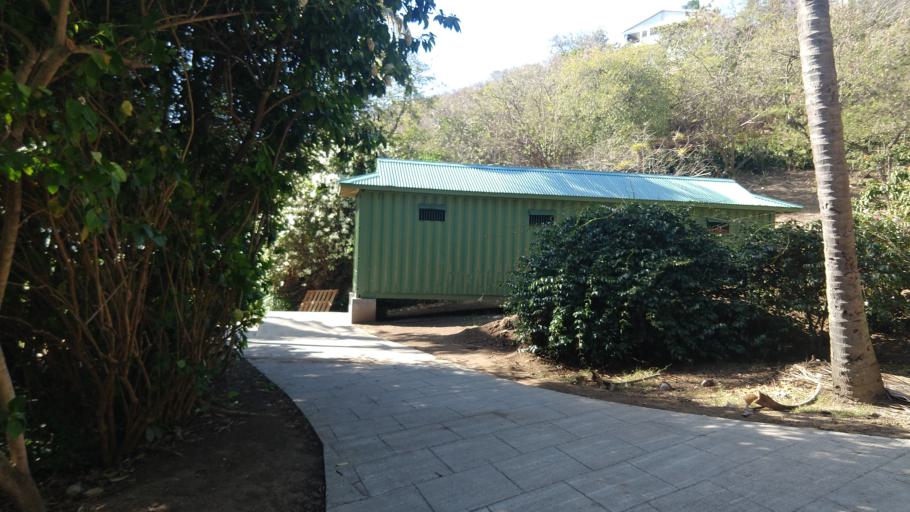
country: VC
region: Grenadines
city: Port Elizabeth
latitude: 12.8820
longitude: -61.1882
